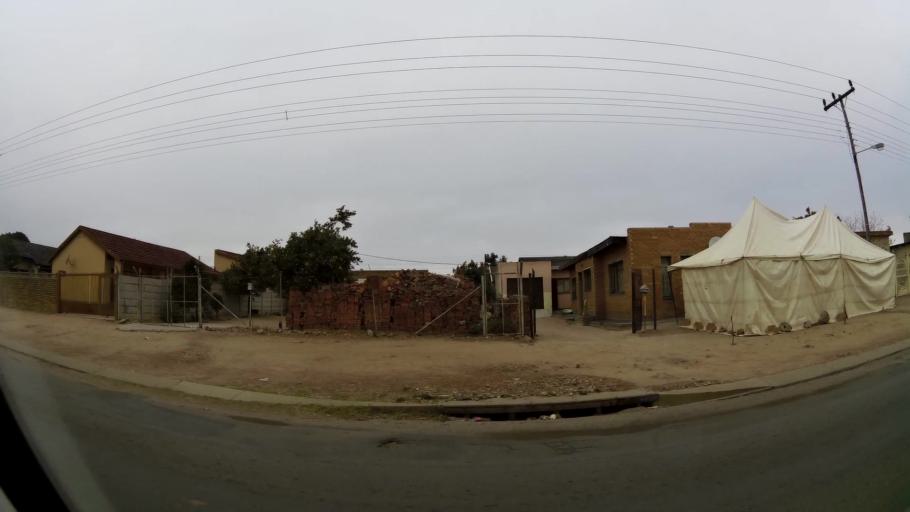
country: ZA
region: Limpopo
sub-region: Capricorn District Municipality
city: Polokwane
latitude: -23.8339
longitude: 29.3855
